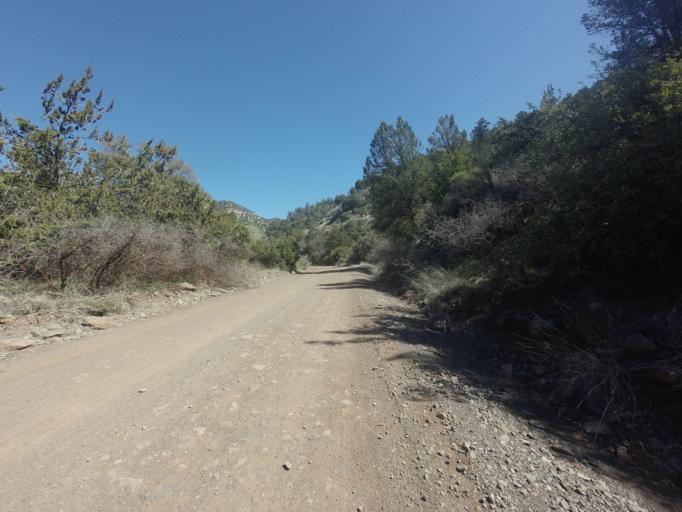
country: US
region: Arizona
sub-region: Gila County
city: Pine
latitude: 34.4009
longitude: -111.6180
